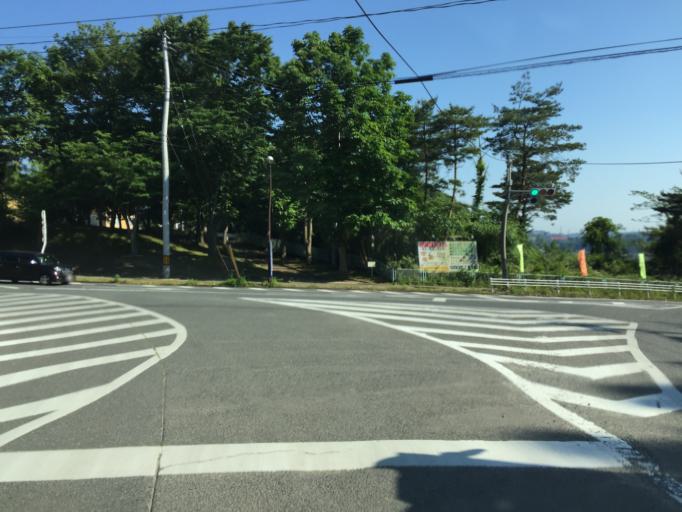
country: JP
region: Fukushima
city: Iwaki
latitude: 36.9649
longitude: 140.8503
